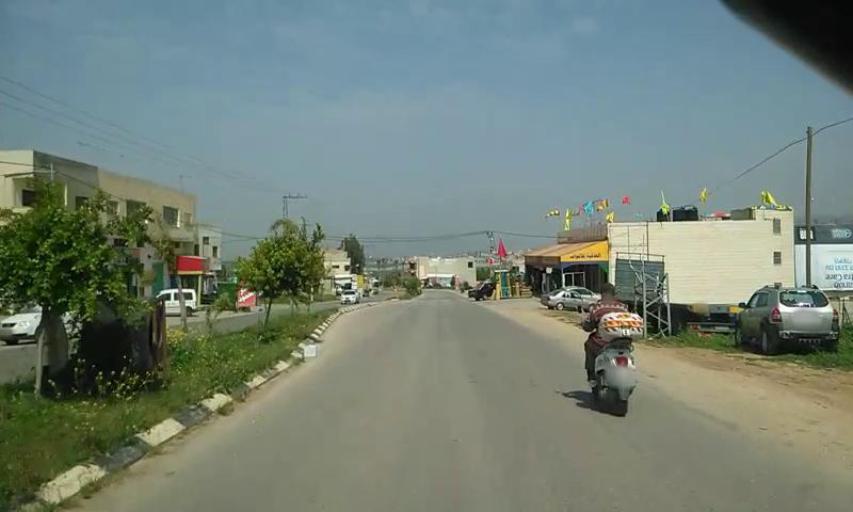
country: PS
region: West Bank
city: Al Jalamah
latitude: 32.4903
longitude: 35.3010
